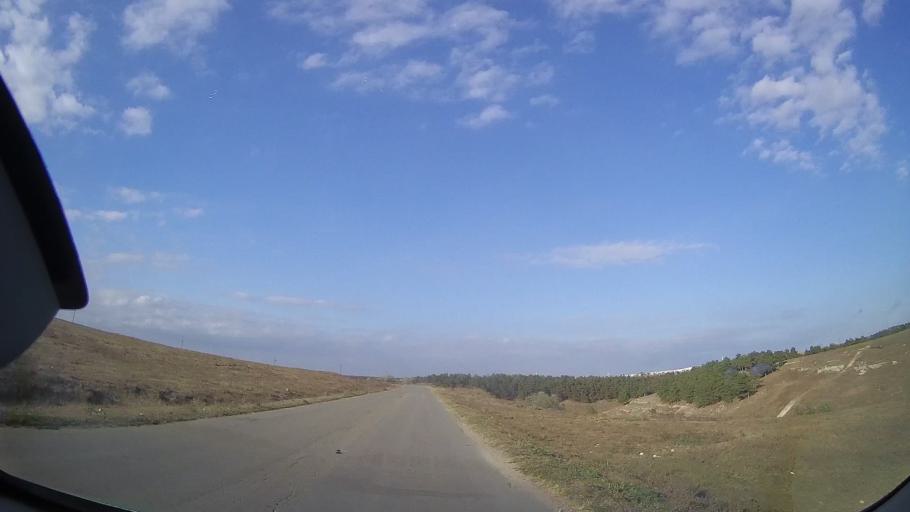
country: RO
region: Constanta
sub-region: Comuna Limanu
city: Limanu
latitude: 43.8071
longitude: 28.5202
